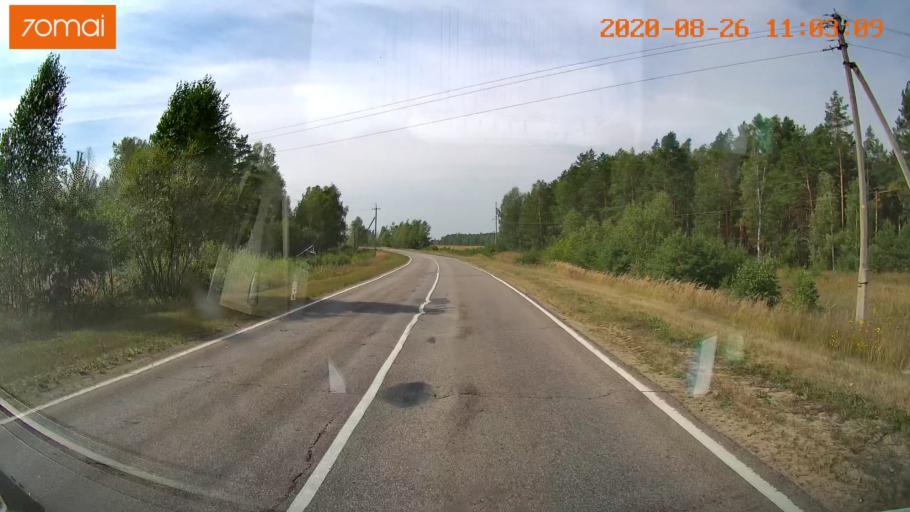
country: RU
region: Rjazan
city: Izhevskoye
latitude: 54.5434
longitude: 41.2160
